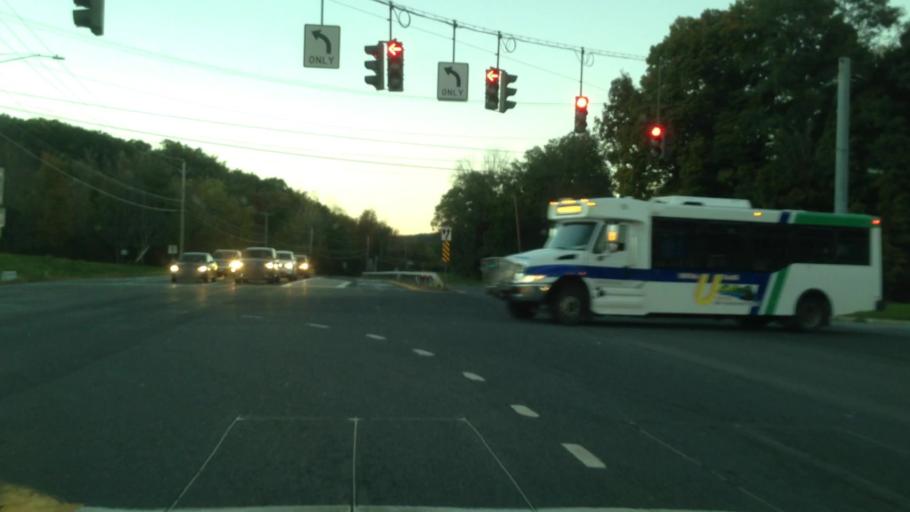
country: US
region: New York
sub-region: Ulster County
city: Highland
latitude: 41.7419
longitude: -73.9643
